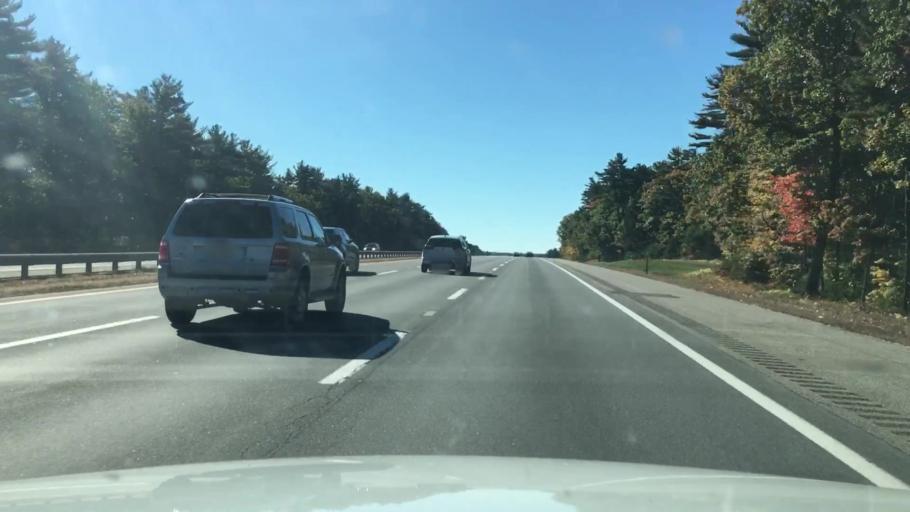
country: US
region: Maine
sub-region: York County
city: Ogunquit
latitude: 43.2803
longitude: -70.6178
